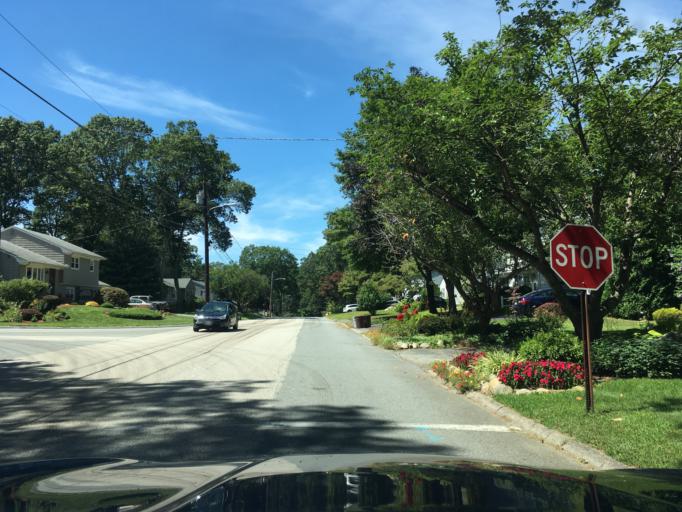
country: US
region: Rhode Island
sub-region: Kent County
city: East Greenwich
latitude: 41.6417
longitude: -71.4733
